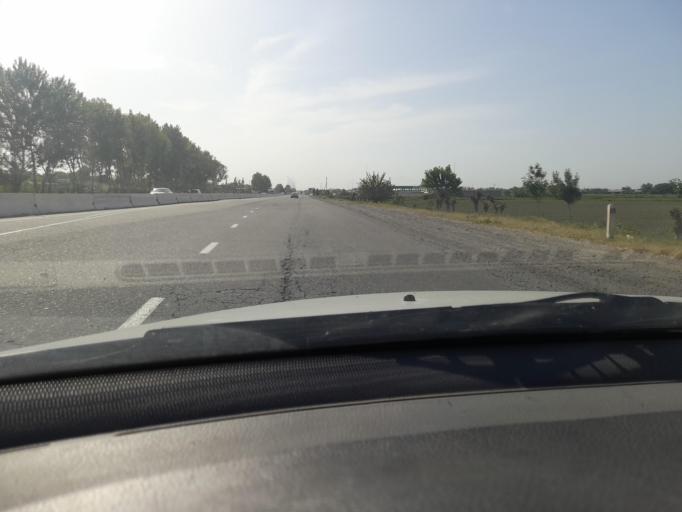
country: UZ
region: Samarqand
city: Kattaqo'rg'on
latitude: 39.9170
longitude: 66.3061
